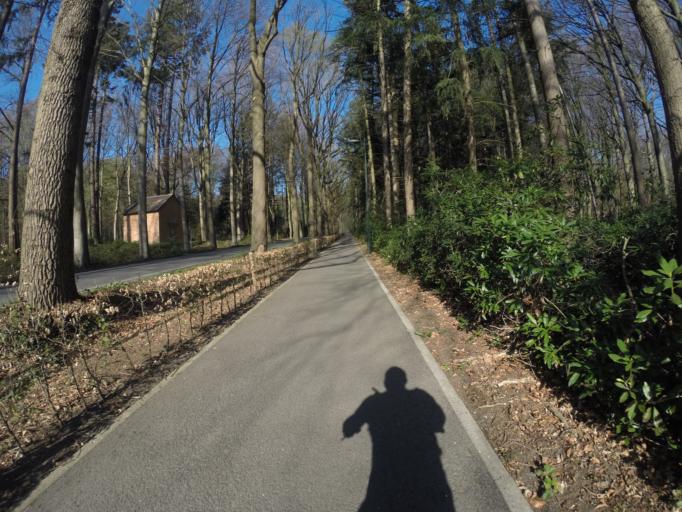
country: BE
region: Flanders
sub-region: Provincie Oost-Vlaanderen
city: Knesselare
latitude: 51.0930
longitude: 3.3893
